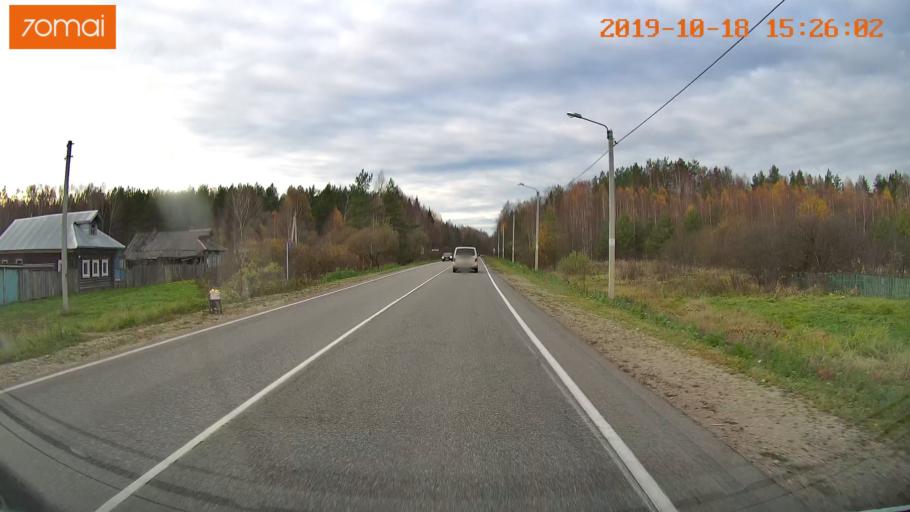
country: RU
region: Vladimir
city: Anopino
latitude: 55.7434
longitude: 40.6943
